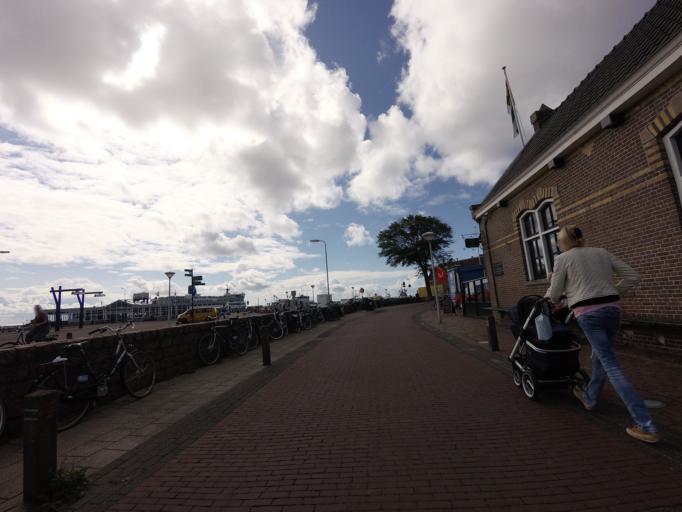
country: NL
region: Friesland
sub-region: Gemeente Terschelling
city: West-Terschelling
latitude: 53.3583
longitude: 5.2161
